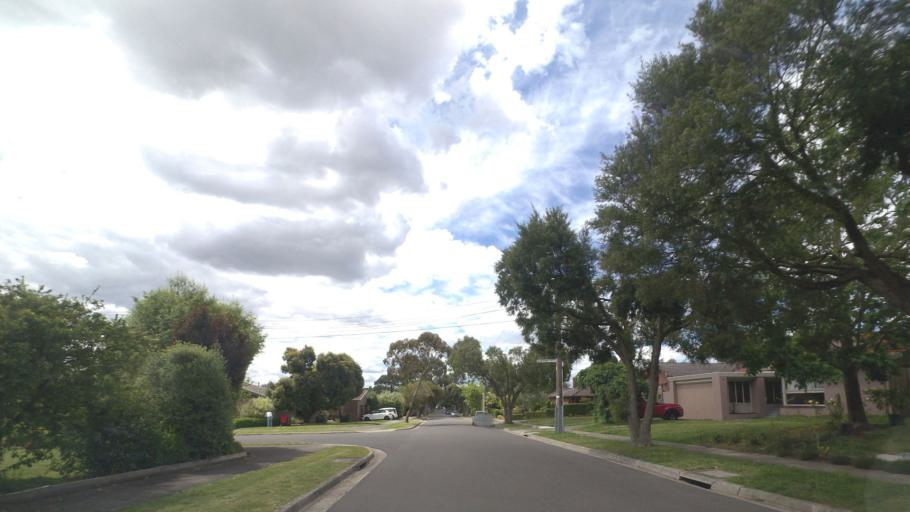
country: AU
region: Victoria
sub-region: Maroondah
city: Heathmont
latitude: -37.8466
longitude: 145.2451
